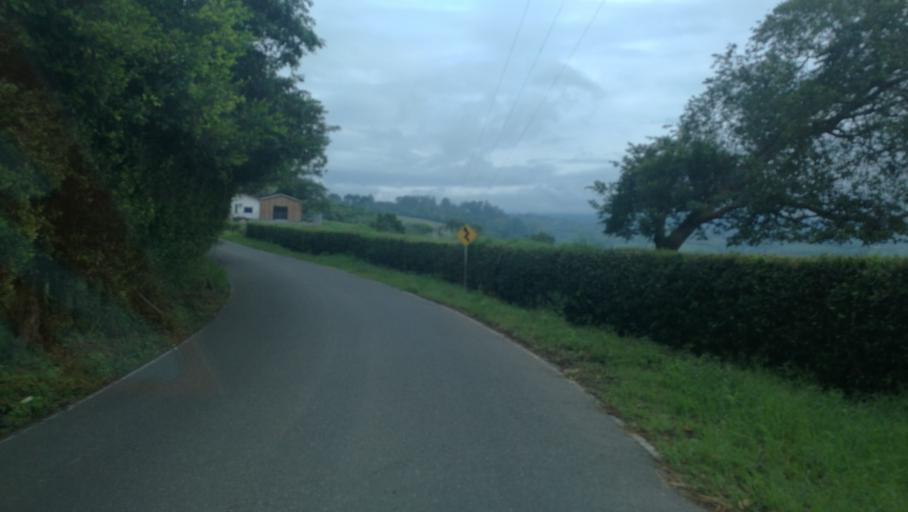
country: CO
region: Quindio
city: Montenegro
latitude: 4.5303
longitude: -75.7738
